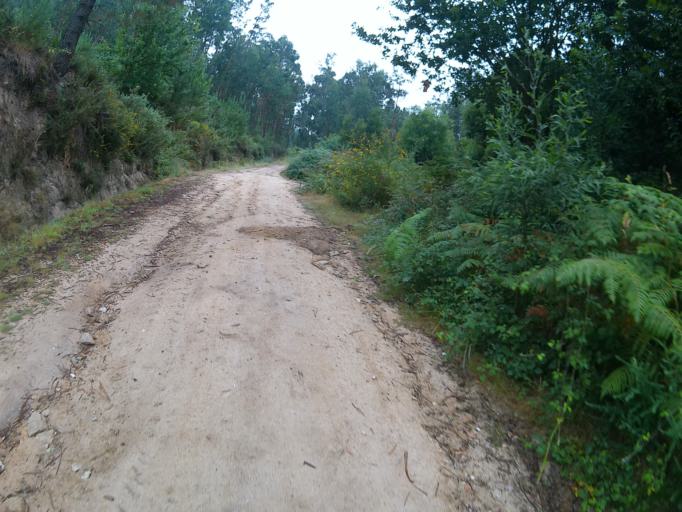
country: PT
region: Viana do Castelo
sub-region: Ponte de Lima
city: Ponte de Lima
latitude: 41.7342
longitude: -8.6031
